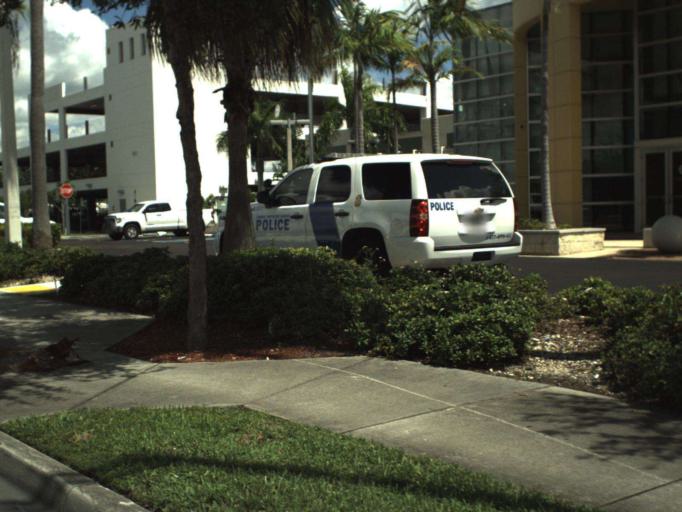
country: US
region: Florida
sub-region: Miami-Dade County
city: Pinewood
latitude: 25.8555
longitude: -80.2094
